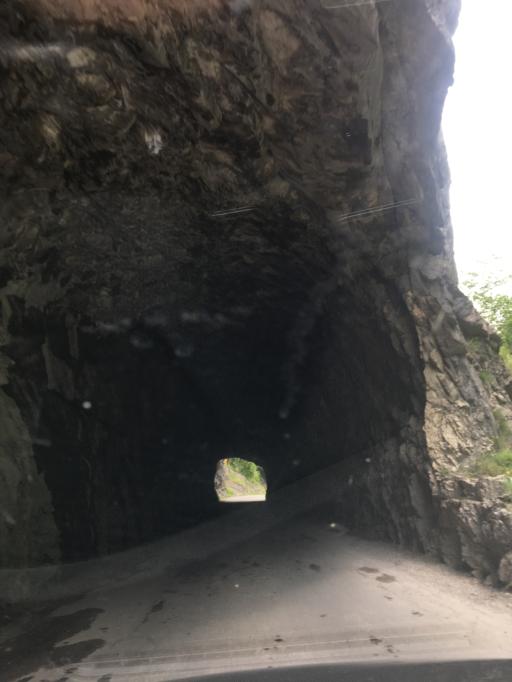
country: XK
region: Pec
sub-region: Komuna e Pejes
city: Peje
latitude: 42.6654
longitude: 20.2283
